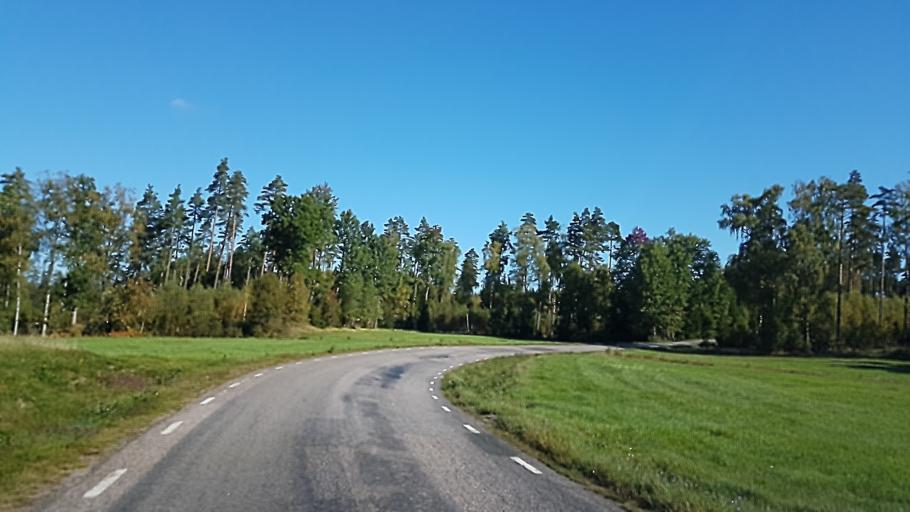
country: SE
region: Kronoberg
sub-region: Ljungby Kommun
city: Ljungby
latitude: 56.8149
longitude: 14.0367
